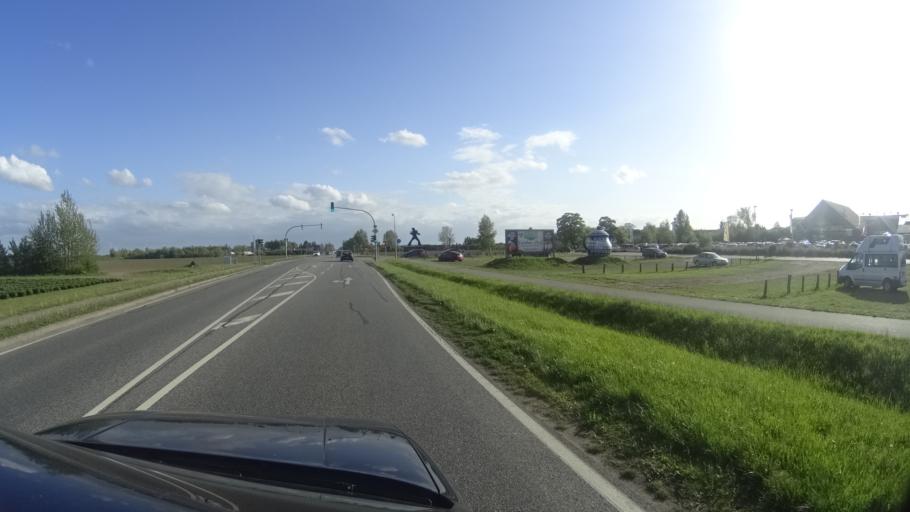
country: DE
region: Mecklenburg-Vorpommern
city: Rovershagen
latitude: 54.1607
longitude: 12.2343
